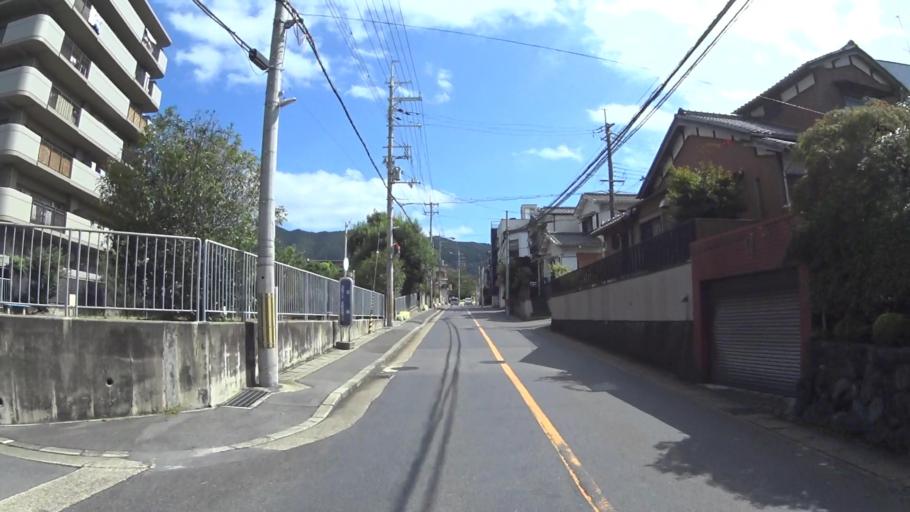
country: JP
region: Kyoto
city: Uji
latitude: 34.9381
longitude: 135.8078
